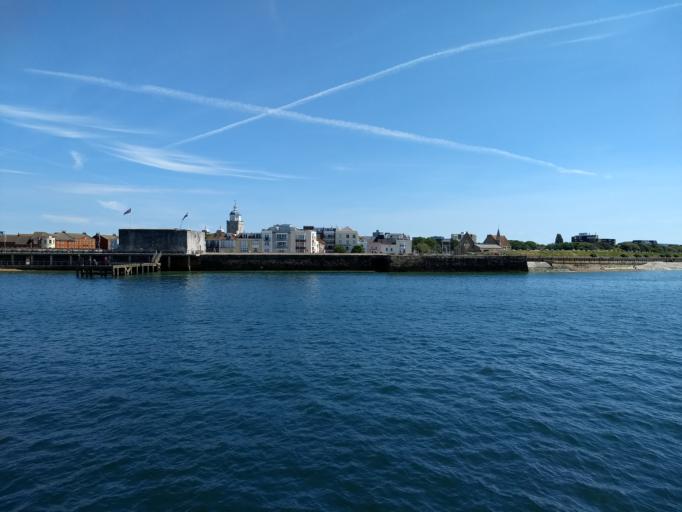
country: GB
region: England
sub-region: Portsmouth
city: Portsmouth
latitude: 50.7882
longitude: -1.1079
